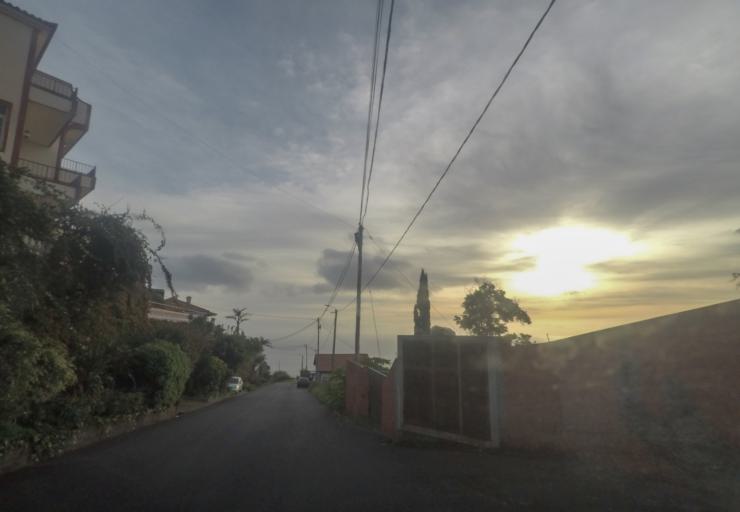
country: PT
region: Madeira
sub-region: Funchal
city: Nossa Senhora do Monte
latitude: 32.6567
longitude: -16.8766
